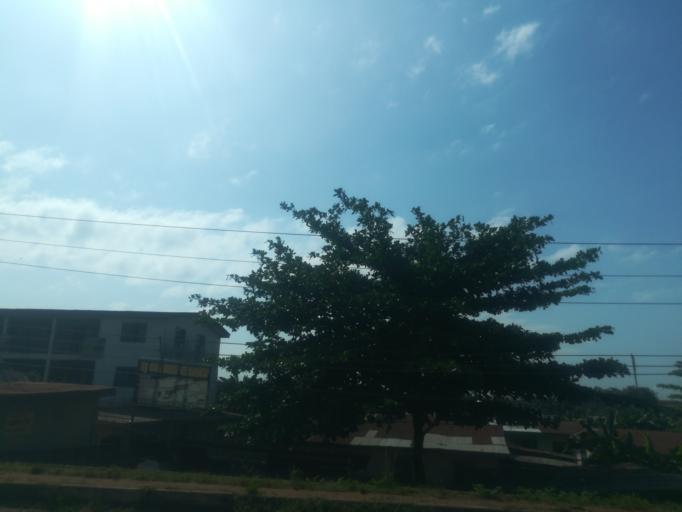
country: NG
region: Oyo
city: Ibadan
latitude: 7.4185
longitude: 3.9667
